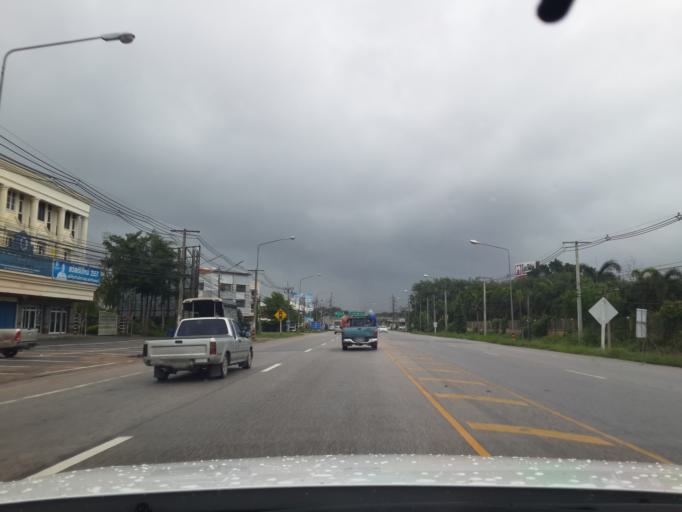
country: TH
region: Songkhla
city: Hat Yai
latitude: 6.9831
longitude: 100.4271
